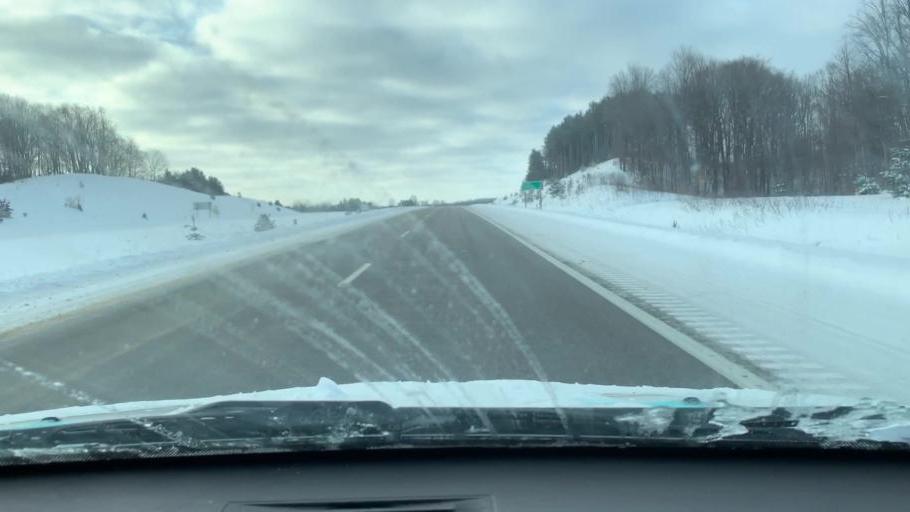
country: US
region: Michigan
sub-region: Wexford County
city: Manton
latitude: 44.3934
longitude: -85.3826
